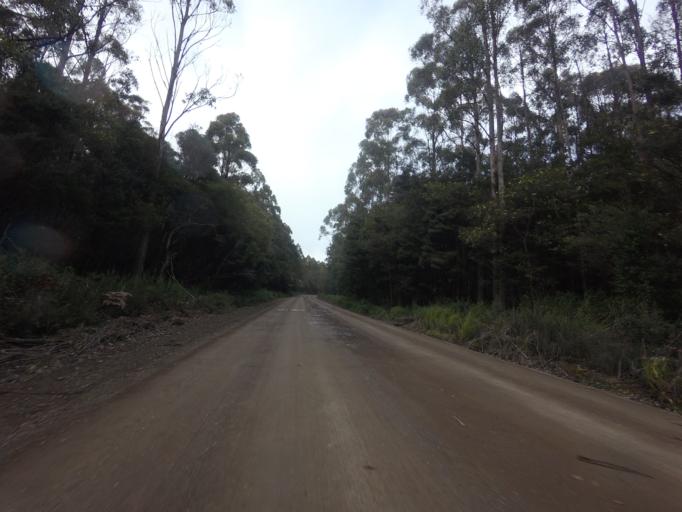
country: AU
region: Tasmania
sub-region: Huon Valley
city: Geeveston
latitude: -43.5189
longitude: 146.8839
